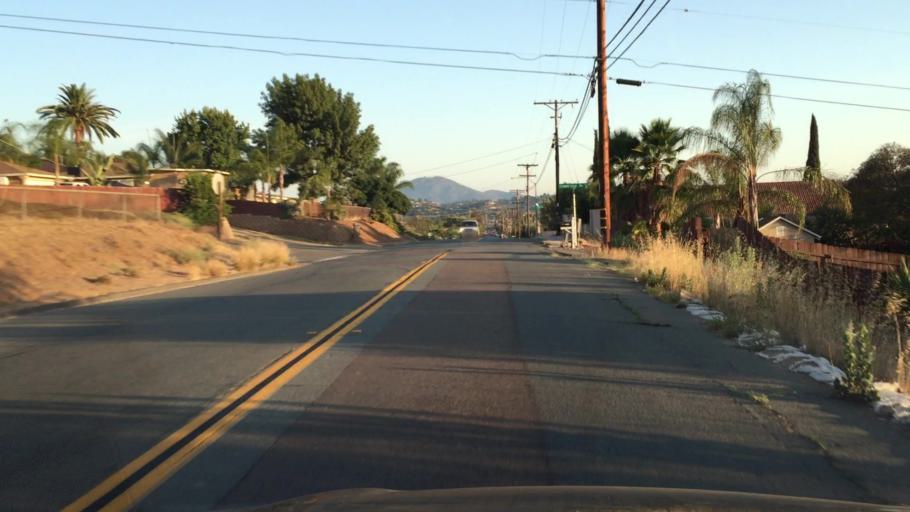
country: US
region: California
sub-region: San Diego County
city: Bostonia
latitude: 32.8171
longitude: -116.9447
